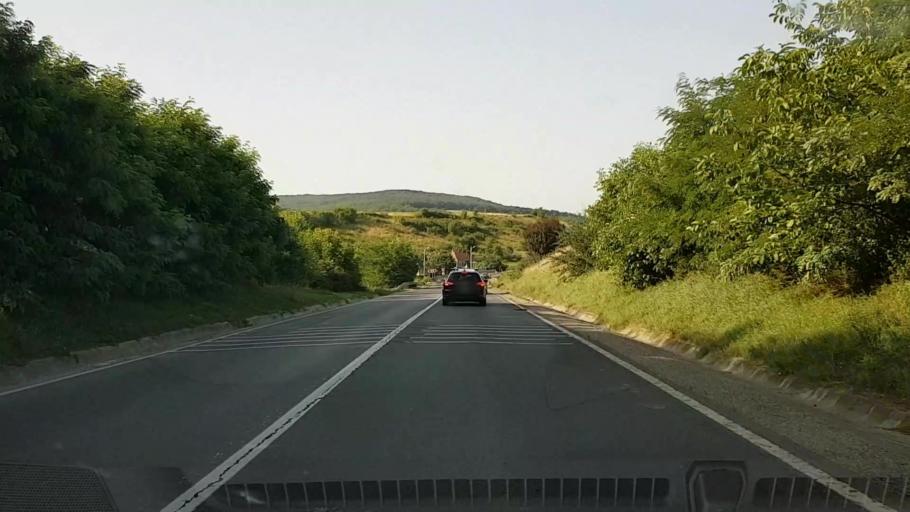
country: RO
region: Alba
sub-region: Comuna Radesti
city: Radesti
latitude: 46.2483
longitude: 23.6876
